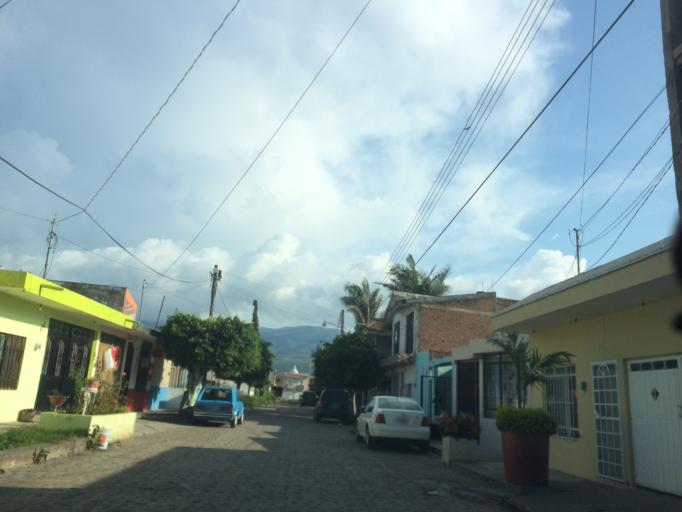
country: MX
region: Nayarit
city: Ixtlan del Rio
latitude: 21.0348
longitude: -104.3869
